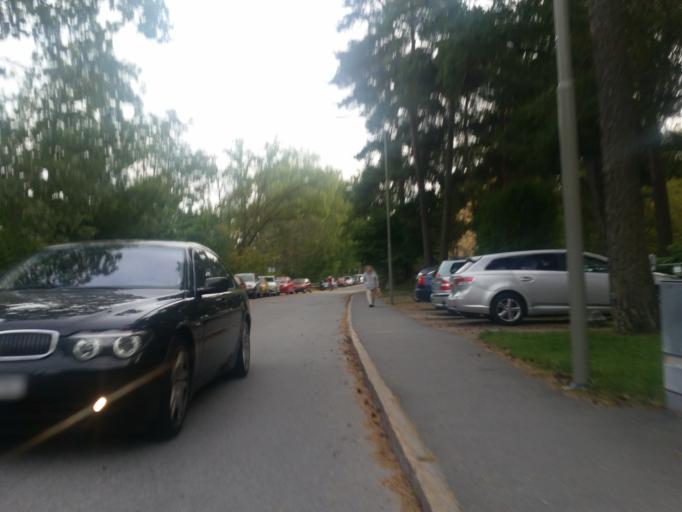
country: SE
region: Stockholm
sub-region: Sundbybergs Kommun
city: Sundbyberg
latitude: 59.3302
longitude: 17.9807
